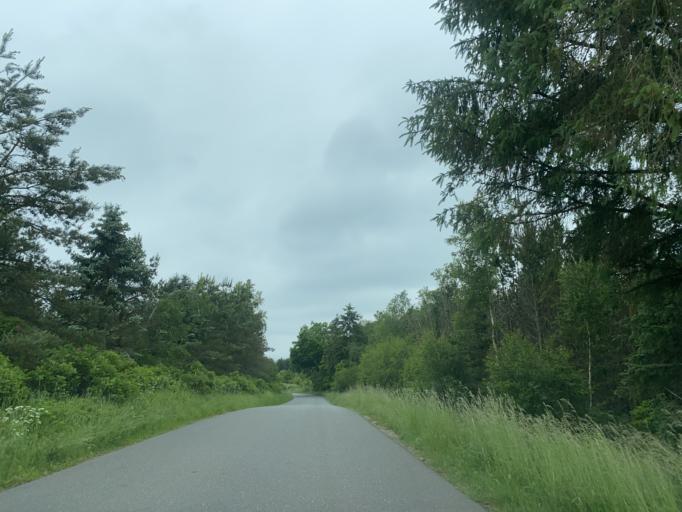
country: DK
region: Central Jutland
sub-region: Viborg Kommune
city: Bjerringbro
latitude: 56.3578
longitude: 9.6317
